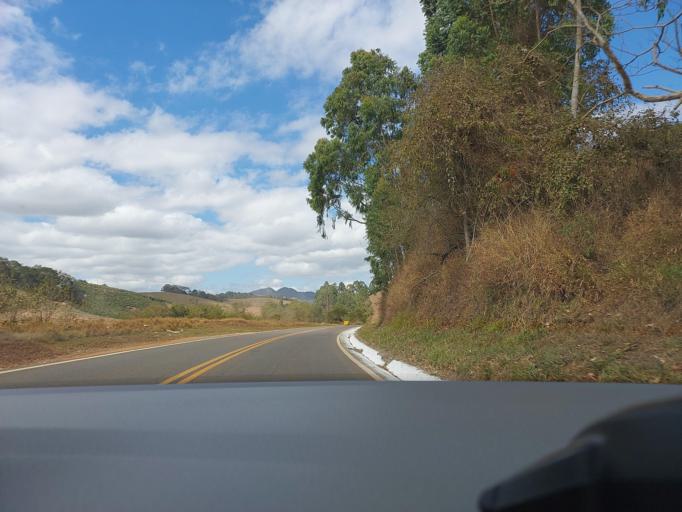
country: BR
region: Minas Gerais
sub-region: Visconde Do Rio Branco
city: Visconde do Rio Branco
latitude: -20.9145
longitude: -42.6406
